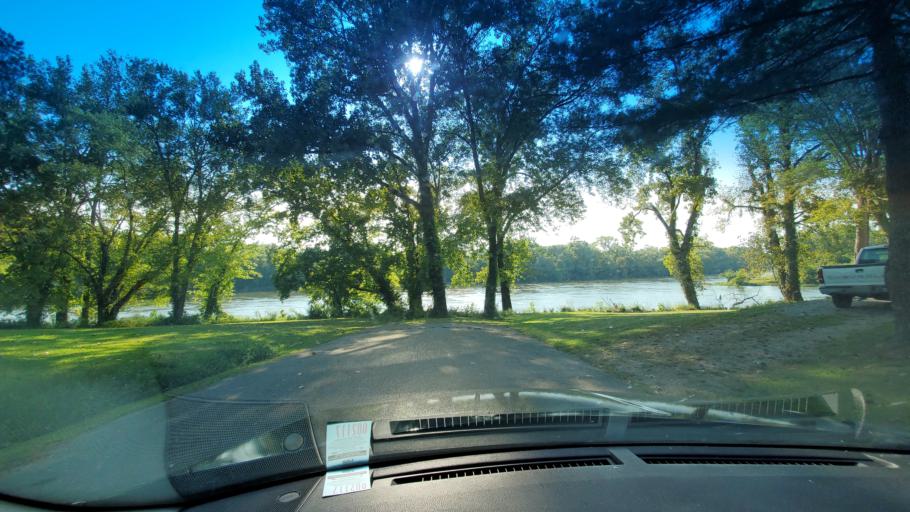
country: US
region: Tennessee
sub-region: Smith County
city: Carthage
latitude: 36.2569
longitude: -85.9581
